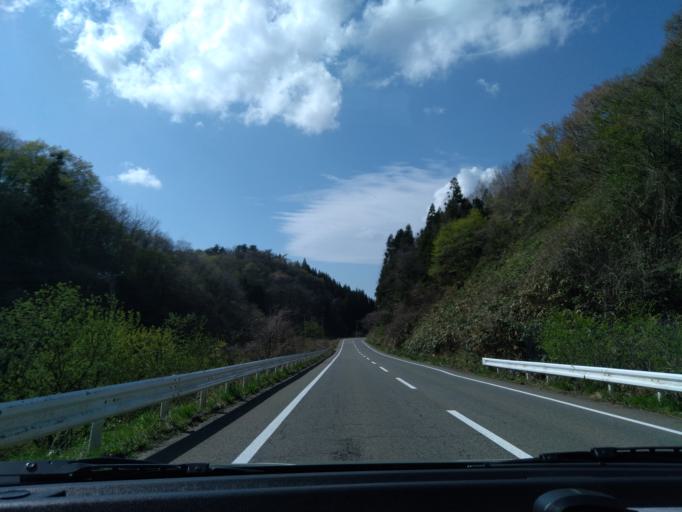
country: JP
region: Akita
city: Akita
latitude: 39.6999
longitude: 140.2188
